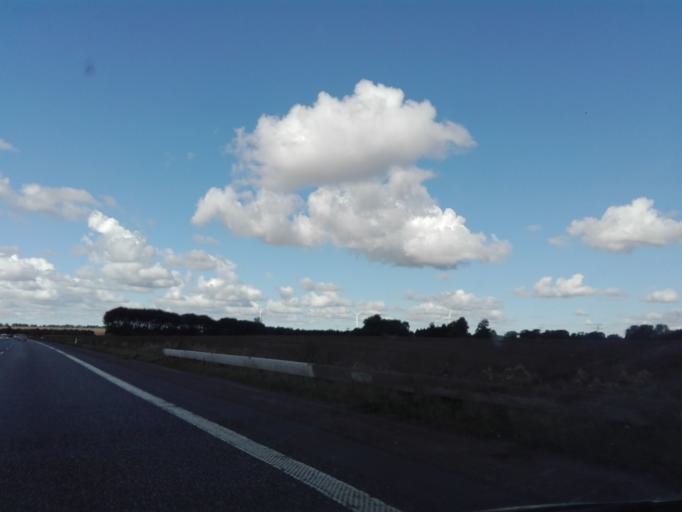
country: DK
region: Central Jutland
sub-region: Randers Kommune
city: Spentrup
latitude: 56.5127
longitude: 9.9675
